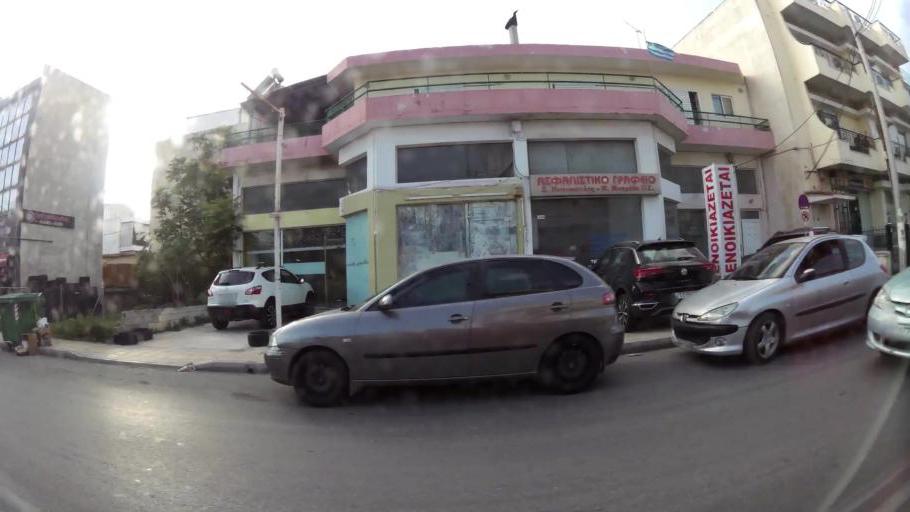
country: GR
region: Attica
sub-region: Nomarchia Anatolikis Attikis
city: Acharnes
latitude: 38.0868
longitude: 23.7304
